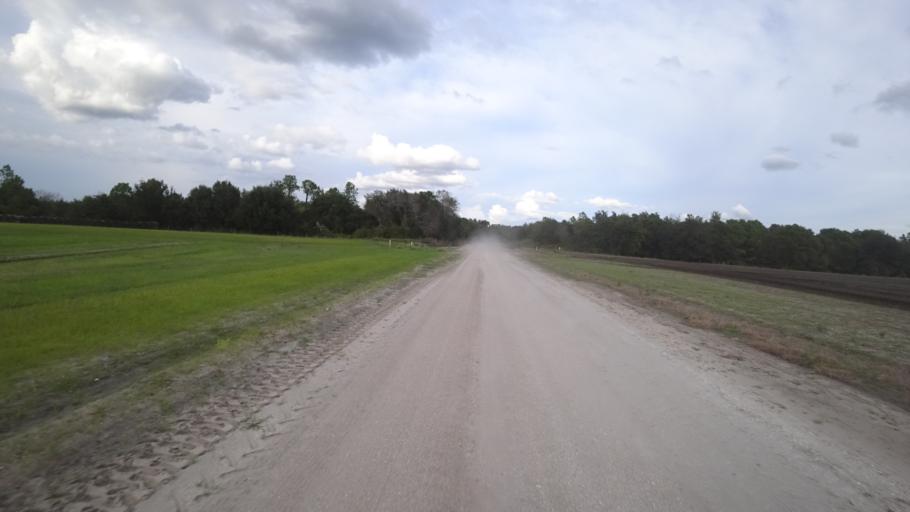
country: US
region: Florida
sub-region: Hillsborough County
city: Wimauma
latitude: 27.5630
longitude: -82.0951
